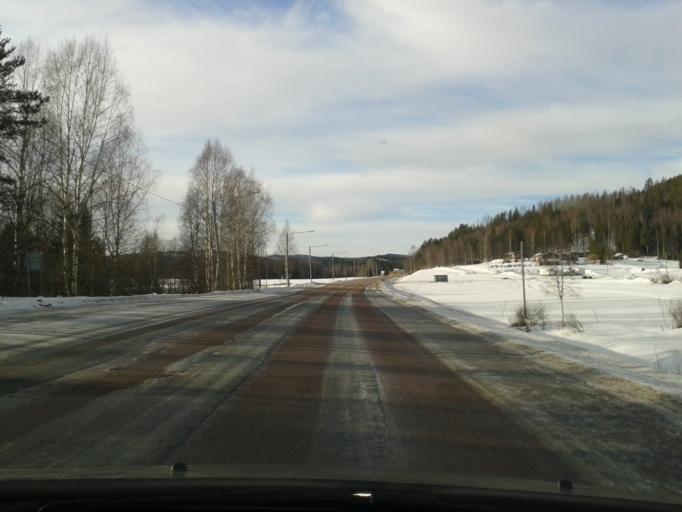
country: SE
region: Vaesternorrland
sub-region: OErnskoeldsviks Kommun
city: Bredbyn
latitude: 63.3904
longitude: 18.3475
